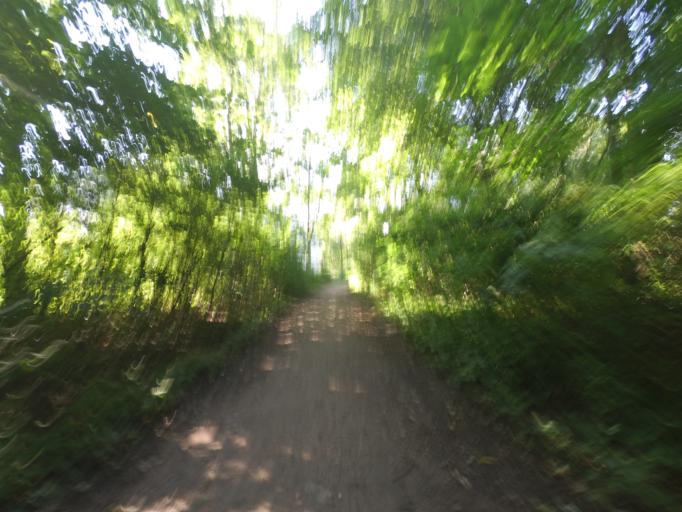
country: DE
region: Hamburg
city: Wandsbek
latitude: 53.5679
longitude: 10.1200
